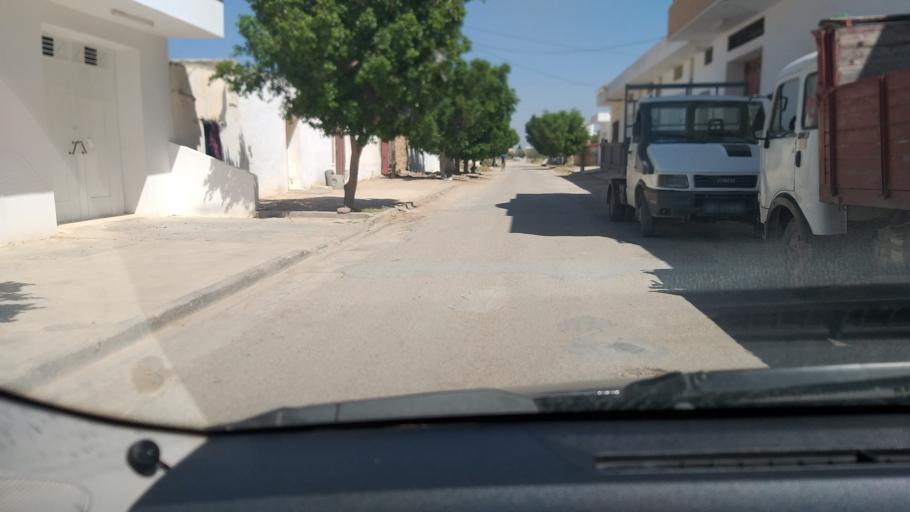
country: TN
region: Al Mahdiyah
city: El Jem
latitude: 35.2909
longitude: 10.7170
